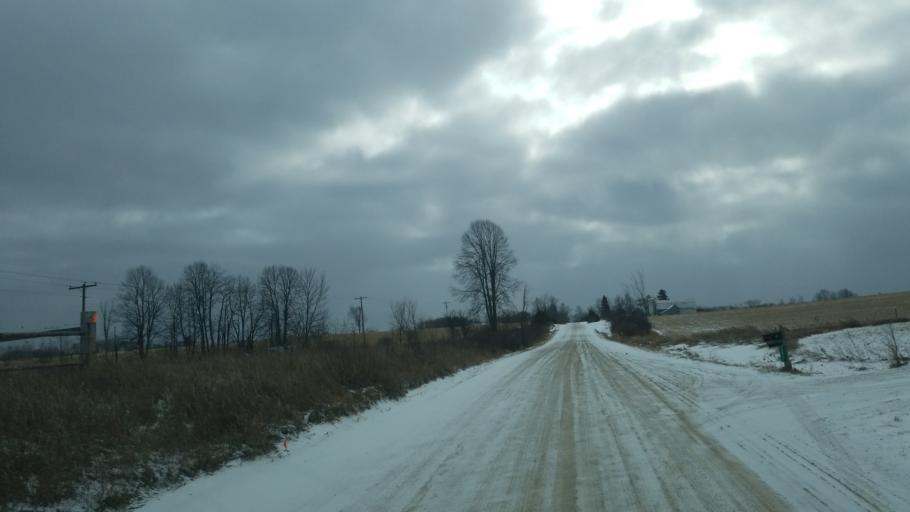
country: US
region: Michigan
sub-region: Osceola County
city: Evart
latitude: 44.0297
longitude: -85.2269
